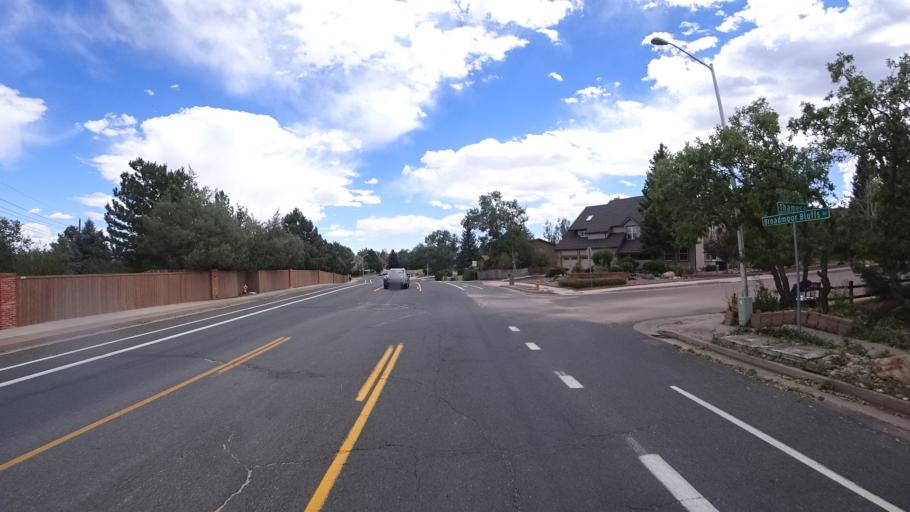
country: US
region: Colorado
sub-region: El Paso County
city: Stratmoor
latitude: 38.7702
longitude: -104.8188
